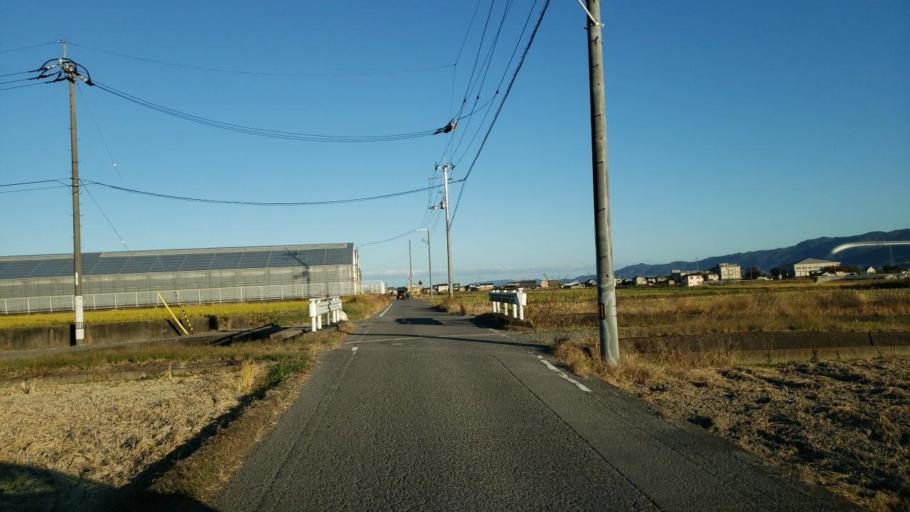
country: JP
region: Tokushima
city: Kamojimacho-jogejima
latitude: 34.0908
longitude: 134.2573
